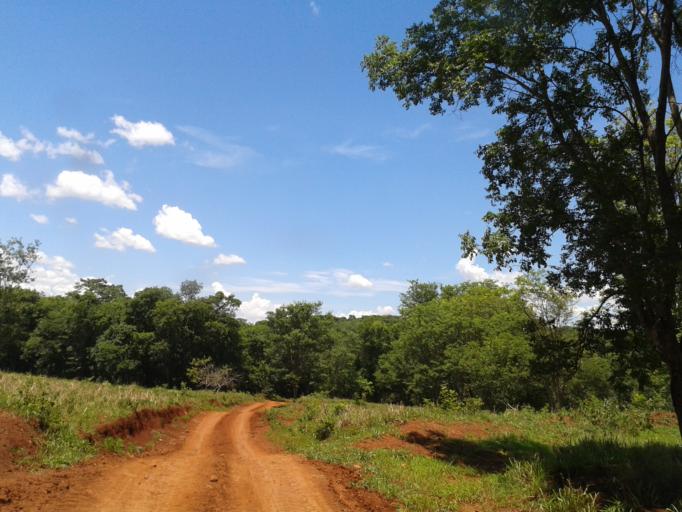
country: BR
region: Minas Gerais
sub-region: Centralina
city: Centralina
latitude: -18.6915
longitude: -49.1802
